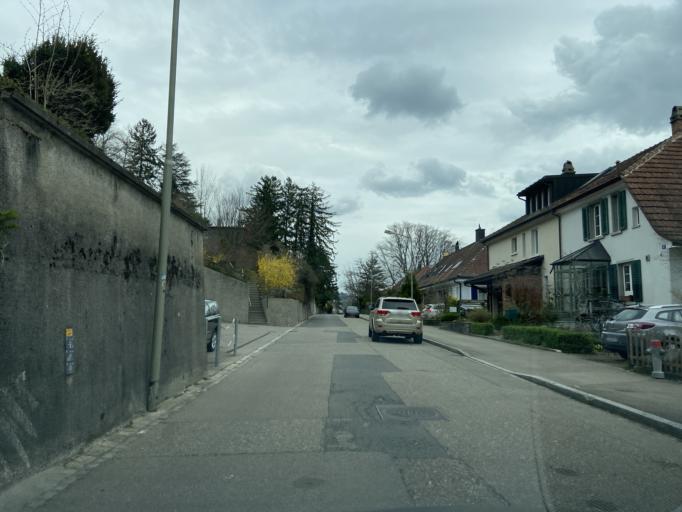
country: CH
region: Zurich
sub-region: Bezirk Winterthur
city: Veltheim (Kreis 5) / Rosenberg
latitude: 47.5104
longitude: 8.7082
